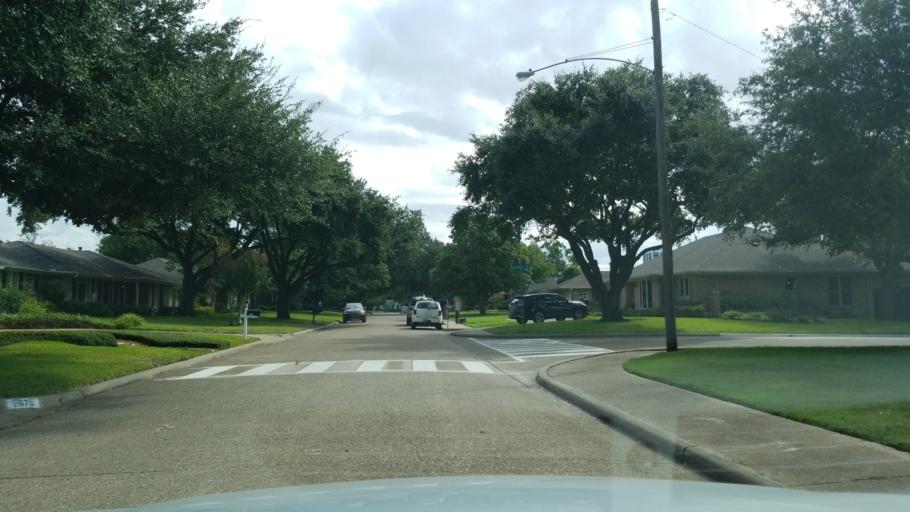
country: US
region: Texas
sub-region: Dallas County
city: Richardson
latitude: 32.9577
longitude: -96.7756
